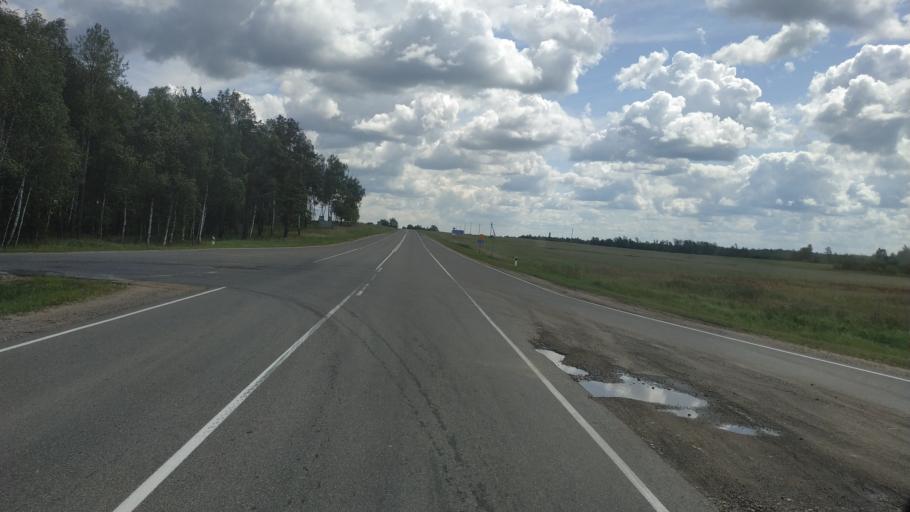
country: BY
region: Mogilev
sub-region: Mahilyowski Rayon
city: Veyno
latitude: 53.8115
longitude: 30.4603
